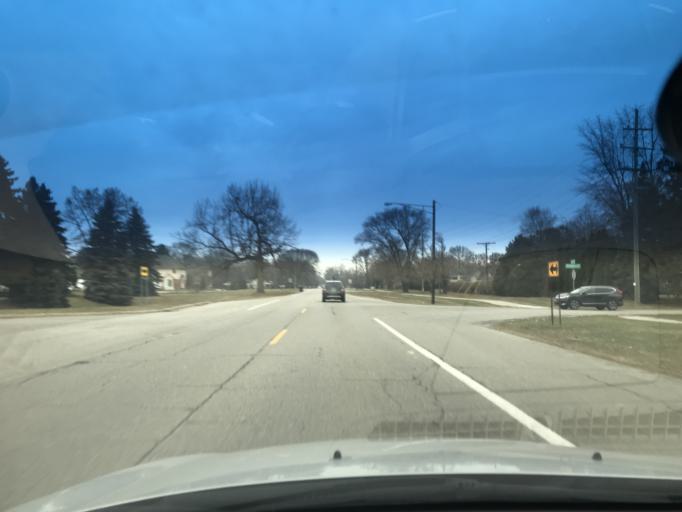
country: US
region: Michigan
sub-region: Macomb County
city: Shelby
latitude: 42.6756
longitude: -83.0538
